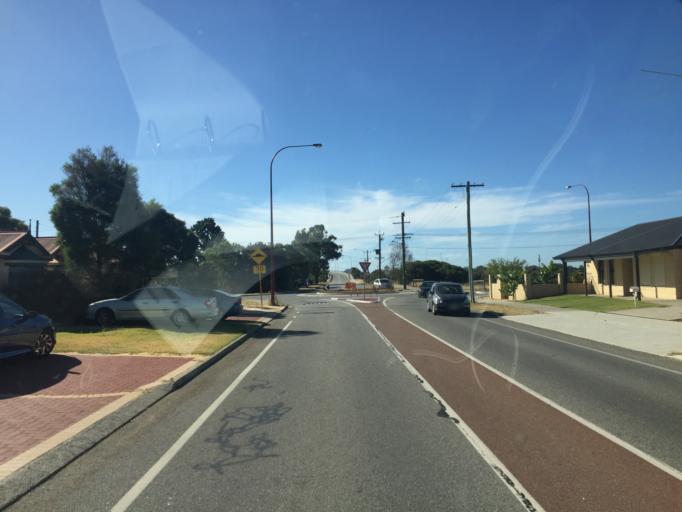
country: AU
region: Western Australia
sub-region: Gosnells
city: Kenwick
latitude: -32.0311
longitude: 115.9759
